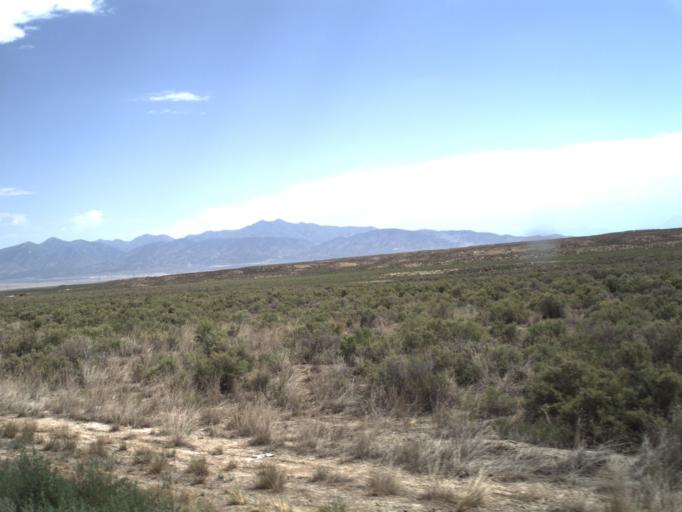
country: US
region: Utah
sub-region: Tooele County
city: Tooele
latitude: 40.1524
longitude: -112.4307
